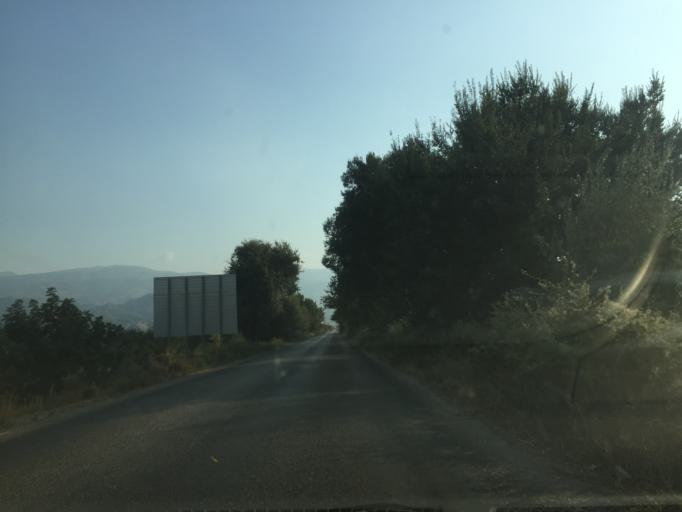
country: TR
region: Manisa
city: Salihli
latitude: 38.5043
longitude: 28.1874
